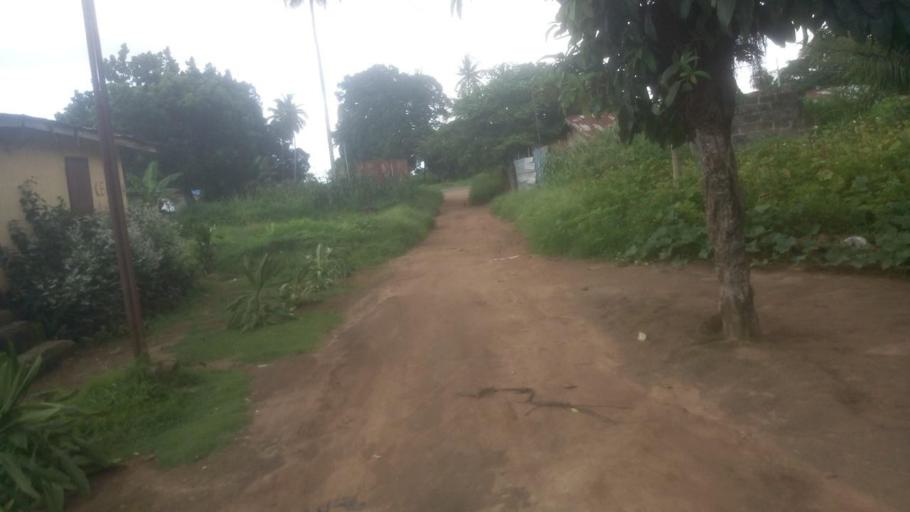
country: SL
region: Northern Province
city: Masoyila
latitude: 8.5852
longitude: -13.1649
